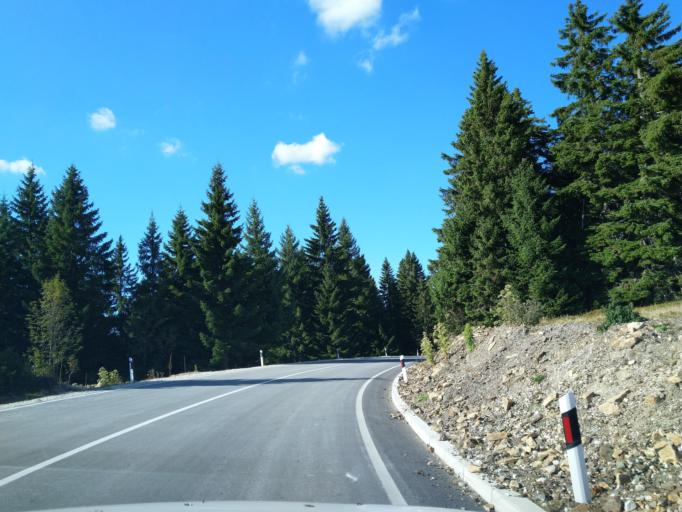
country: RS
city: Sokolovica
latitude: 43.3114
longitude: 20.2945
